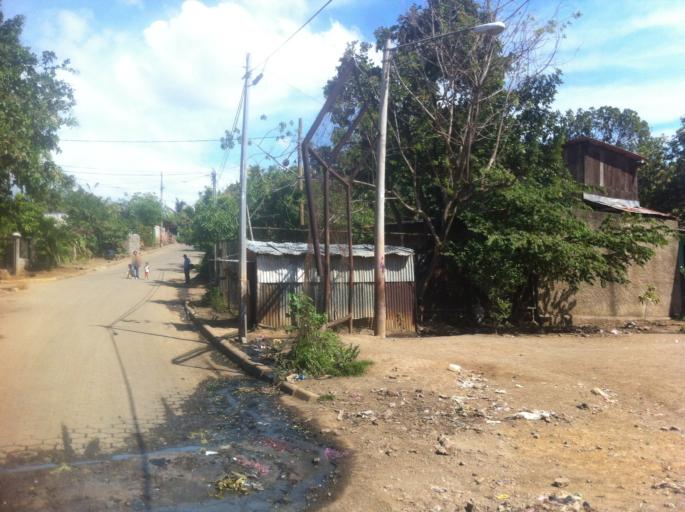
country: NI
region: Managua
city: Ciudad Sandino
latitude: 12.0761
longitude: -86.3299
